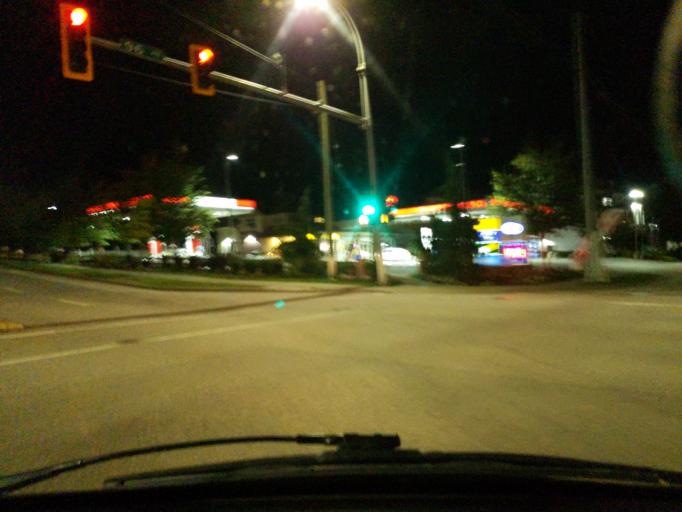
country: CA
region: British Columbia
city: Pitt Meadows
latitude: 49.1769
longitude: -122.6904
